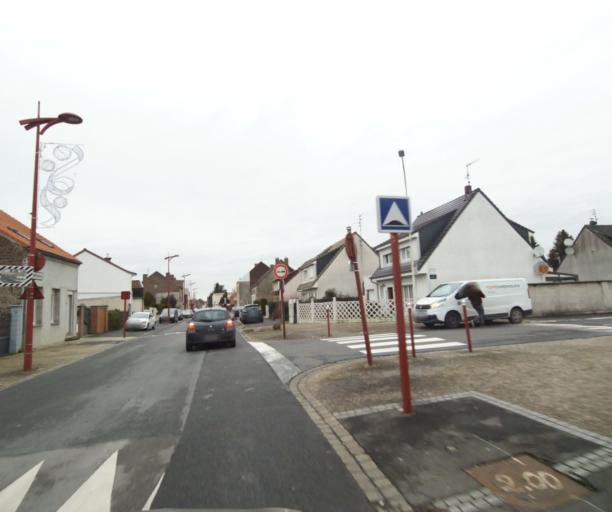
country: FR
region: Nord-Pas-de-Calais
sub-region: Departement du Nord
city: Petite-Foret
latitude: 50.3676
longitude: 3.4796
